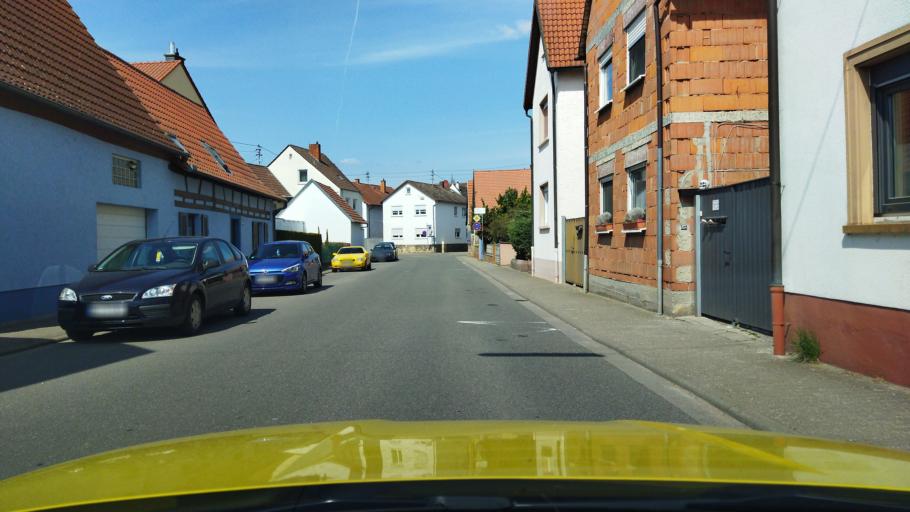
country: DE
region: Rheinland-Pfalz
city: Gommersheim
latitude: 49.3037
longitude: 8.2624
